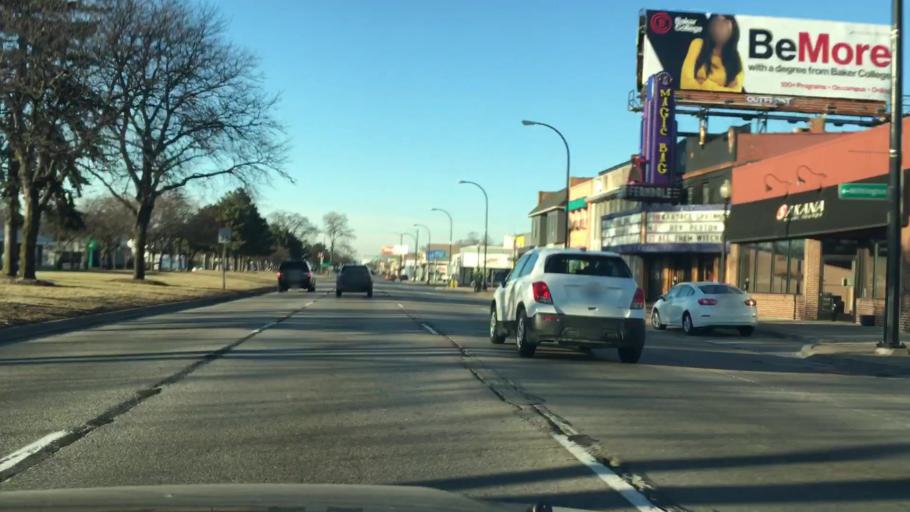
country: US
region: Michigan
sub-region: Oakland County
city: Ferndale
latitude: 42.4615
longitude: -83.1350
